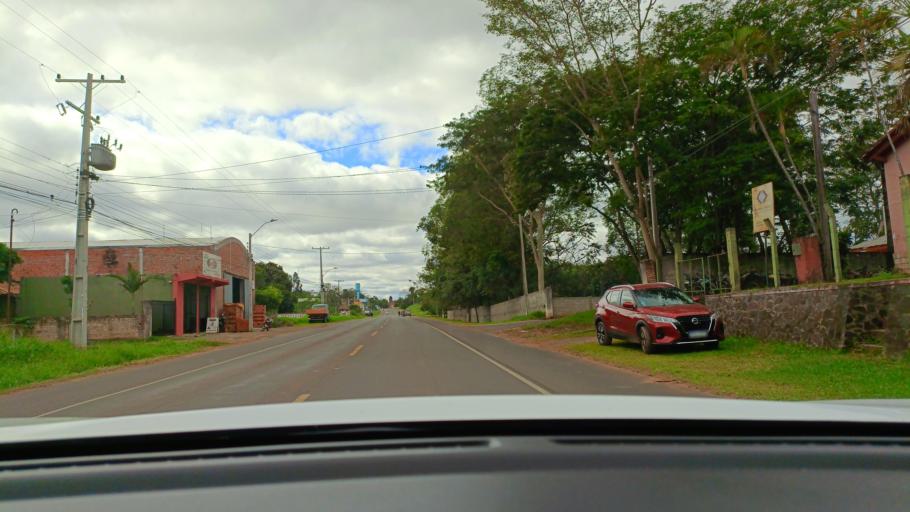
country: PY
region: San Pedro
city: Guayaybi
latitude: -24.6777
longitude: -56.4613
